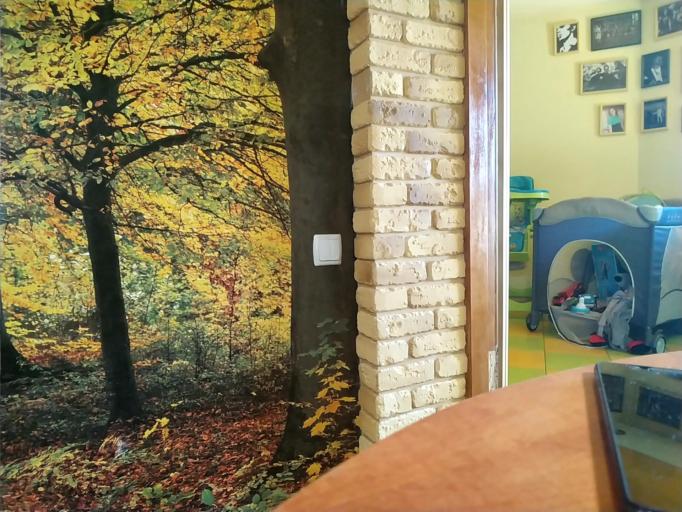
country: RU
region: Tverskaya
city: Velikooktyabr'skiy
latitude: 57.5141
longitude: 34.0534
